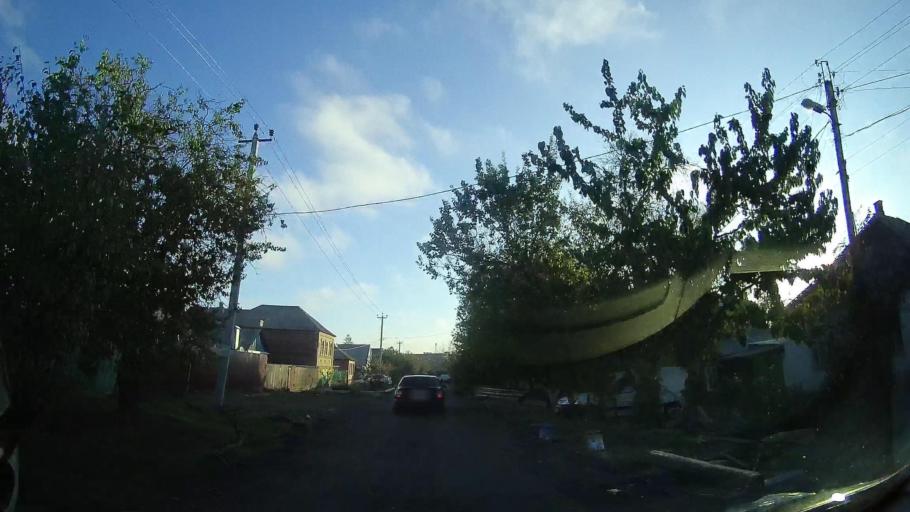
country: RU
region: Rostov
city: Severnyy
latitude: 47.2656
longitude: 39.6762
